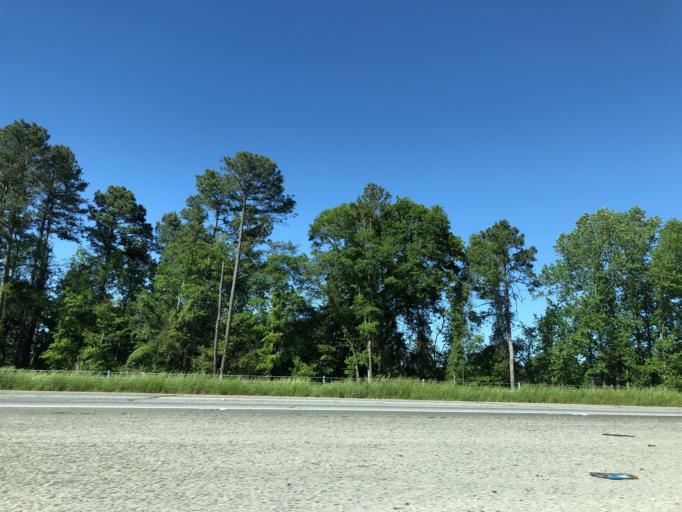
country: US
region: Georgia
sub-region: Clarke County
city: Country Club Estates
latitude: 33.9712
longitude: -83.4074
